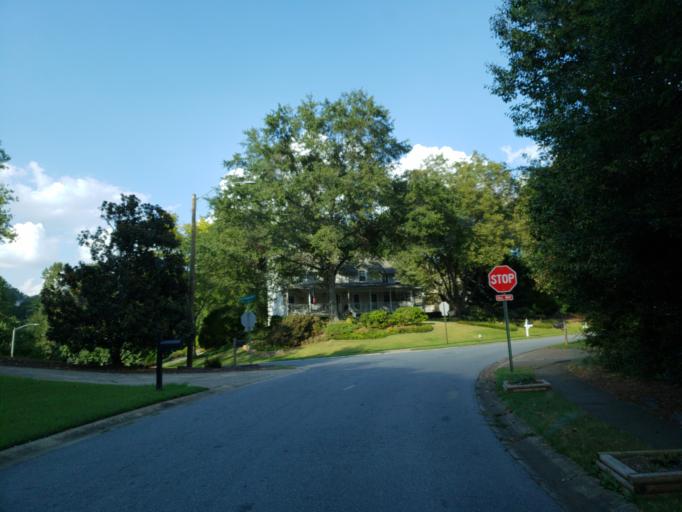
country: US
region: Georgia
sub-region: Cherokee County
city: Woodstock
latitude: 34.0594
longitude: -84.4499
